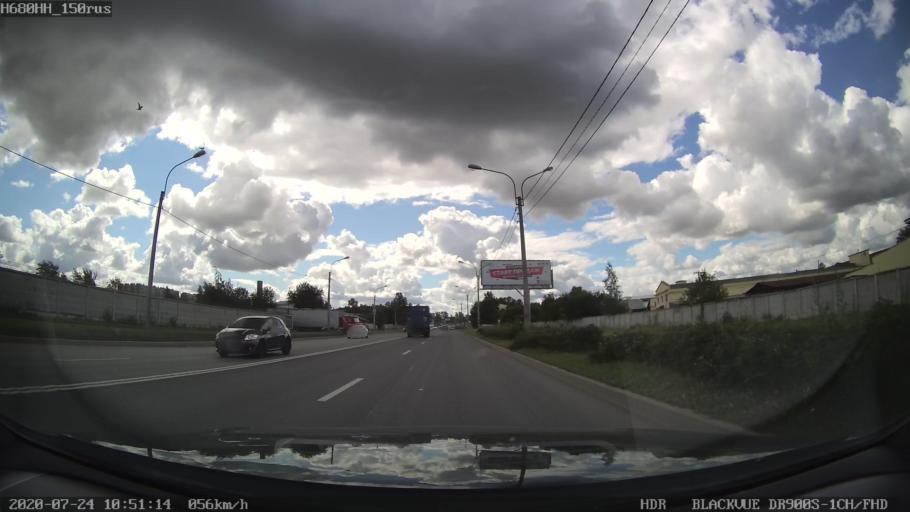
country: RU
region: St.-Petersburg
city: Admiralteisky
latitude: 59.8929
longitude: 30.3012
